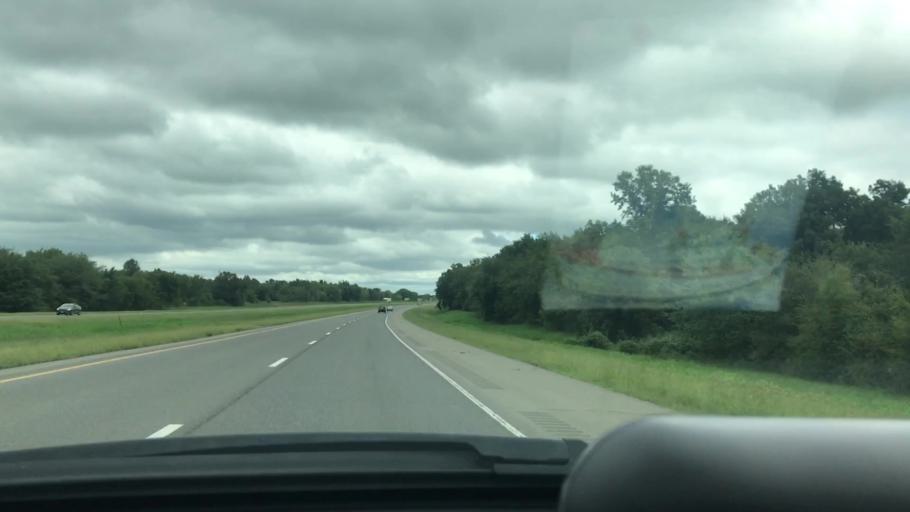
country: US
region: Oklahoma
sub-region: McIntosh County
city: Checotah
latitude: 35.5829
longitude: -95.4903
